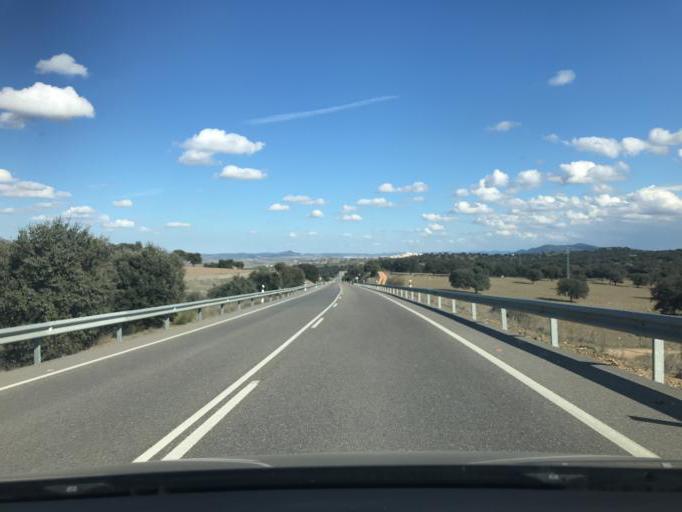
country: ES
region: Andalusia
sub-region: Province of Cordoba
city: Fuente Obejuna
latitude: 38.2592
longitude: -5.4690
